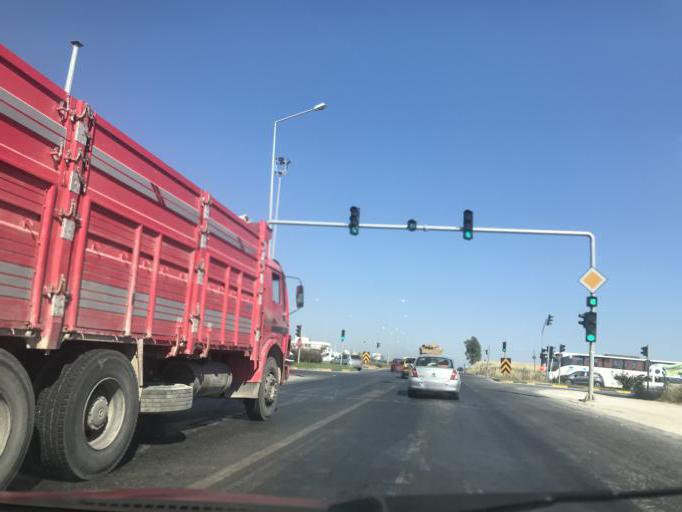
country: TR
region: Antalya
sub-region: Manavgat
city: Side
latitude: 36.8050
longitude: 31.3908
